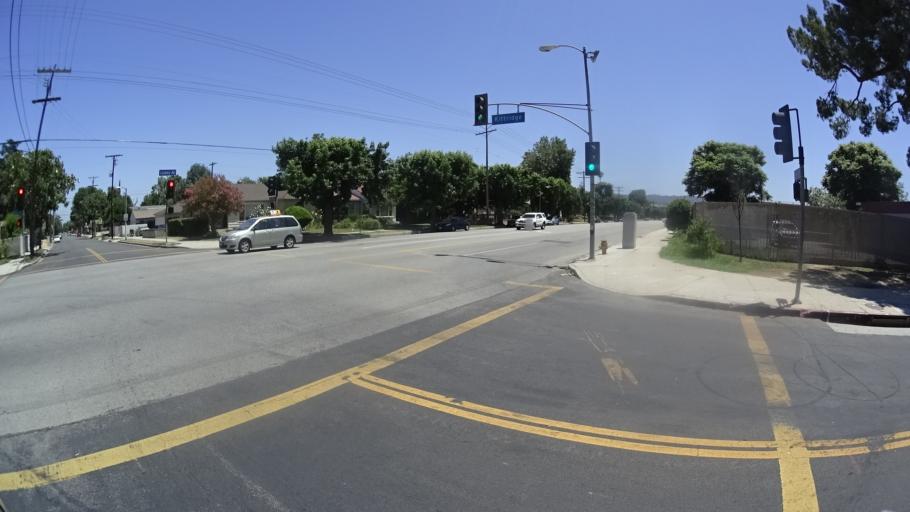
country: US
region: California
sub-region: Los Angeles County
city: Northridge
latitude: 34.1904
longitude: -118.5275
